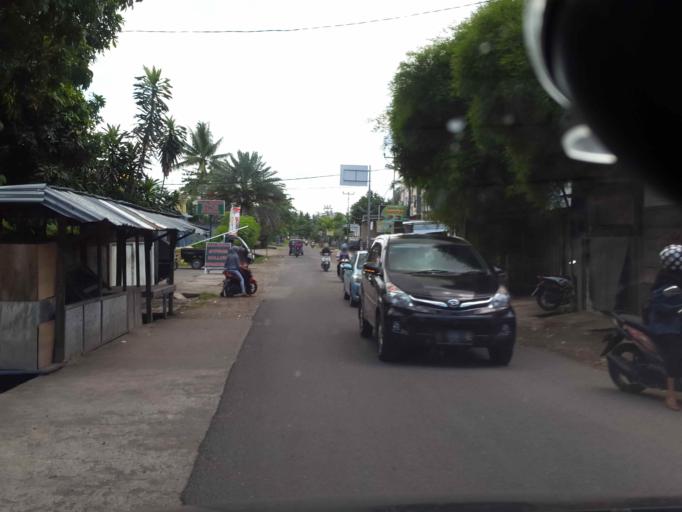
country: ID
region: West Nusa Tenggara
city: Mambalan
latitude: -8.5415
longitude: 116.0723
